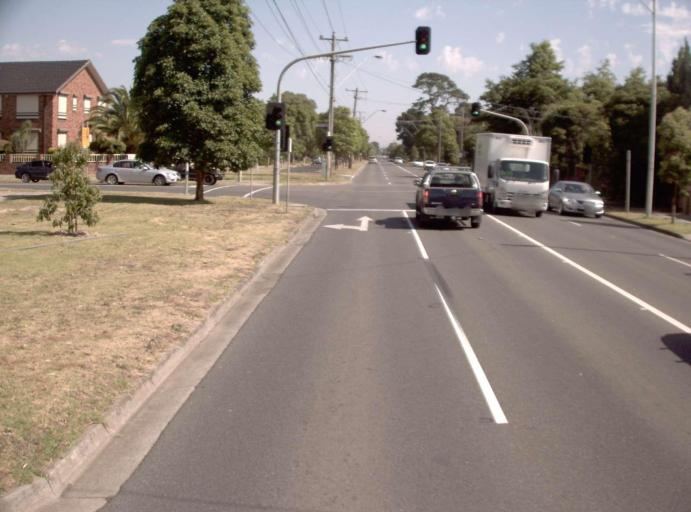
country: AU
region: Victoria
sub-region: Monash
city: Mulgrave
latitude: -37.9127
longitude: 145.1880
